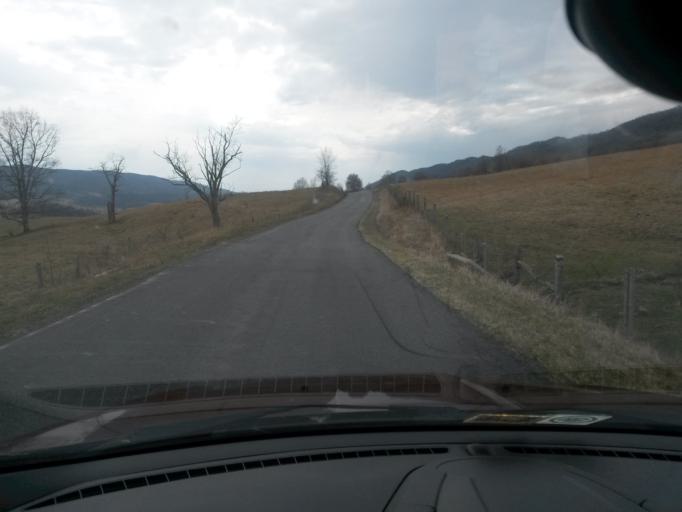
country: US
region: Virginia
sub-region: Highland County
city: Monterey
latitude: 38.4077
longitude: -79.6506
